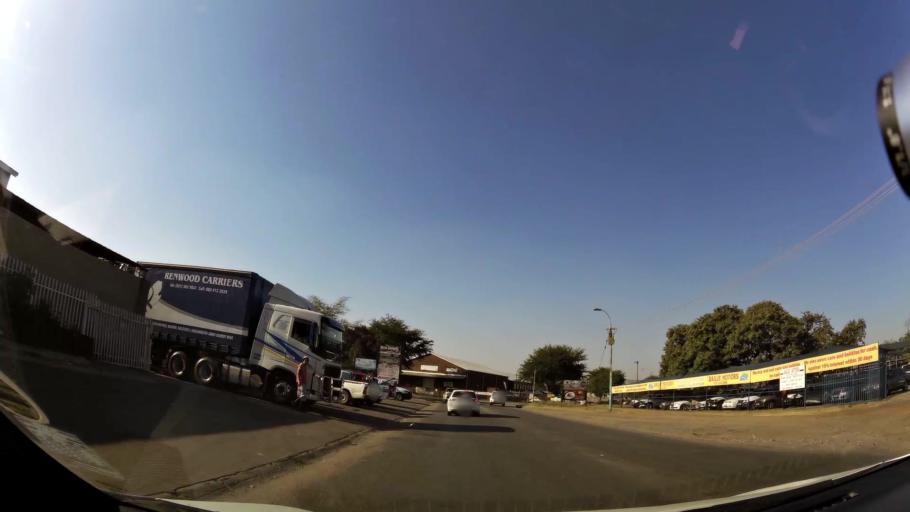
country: ZA
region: North-West
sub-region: Bojanala Platinum District Municipality
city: Rustenburg
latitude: -25.6660
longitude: 27.2609
